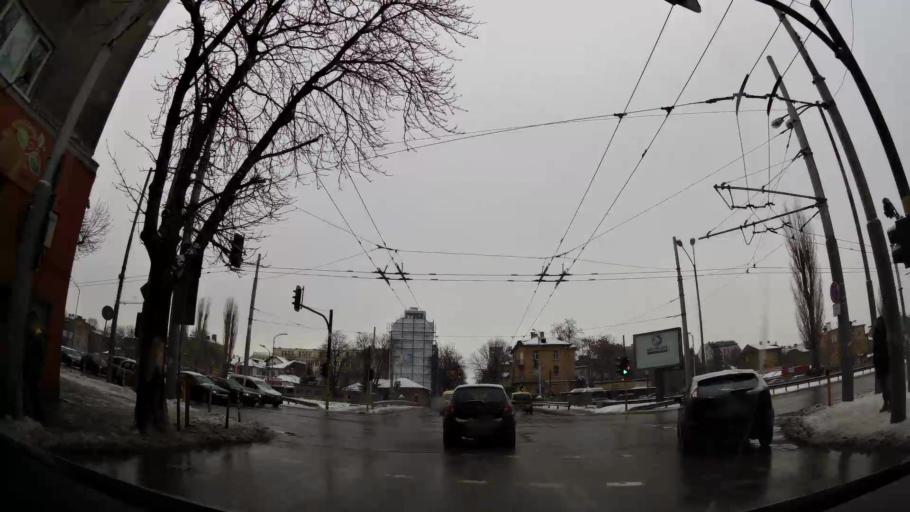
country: BG
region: Sofia-Capital
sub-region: Stolichna Obshtina
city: Sofia
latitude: 42.7041
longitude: 23.3289
